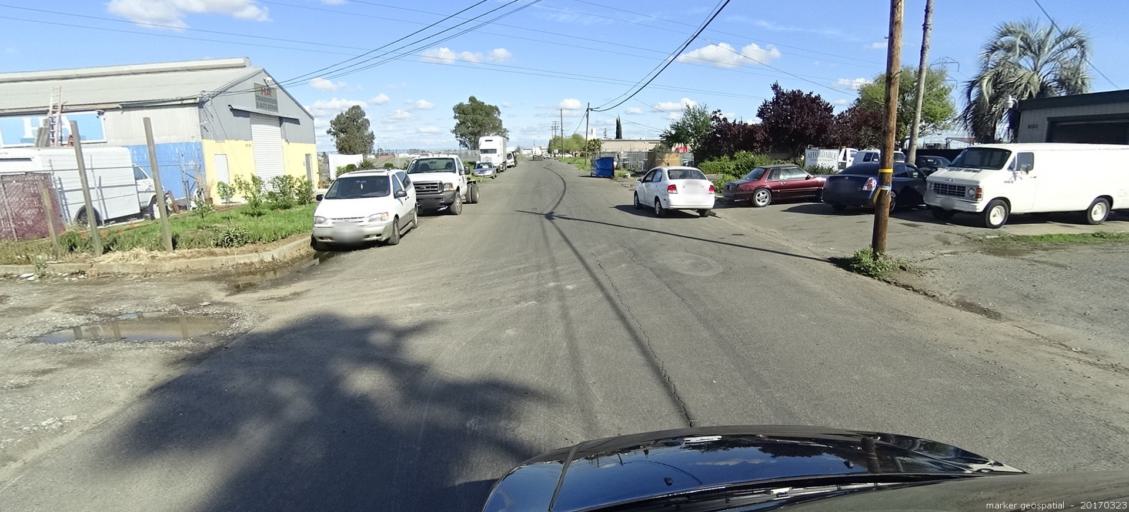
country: US
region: California
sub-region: Sacramento County
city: Florin
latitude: 38.5215
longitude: -121.3887
